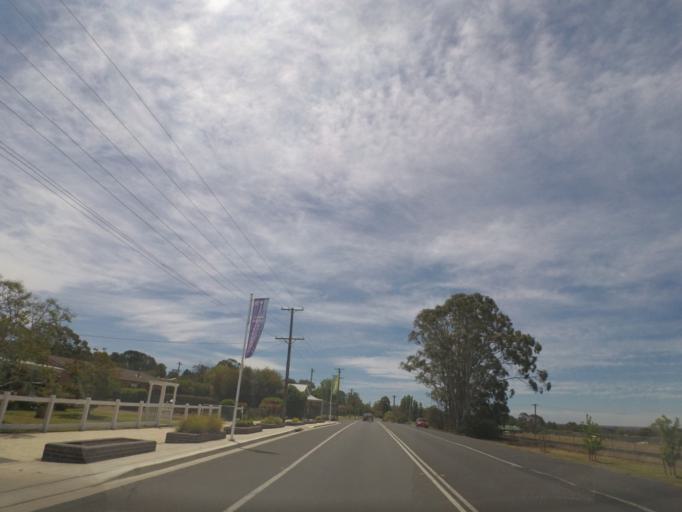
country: AU
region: New South Wales
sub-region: Wollondilly
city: Buxton
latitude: -34.2890
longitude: 150.5792
